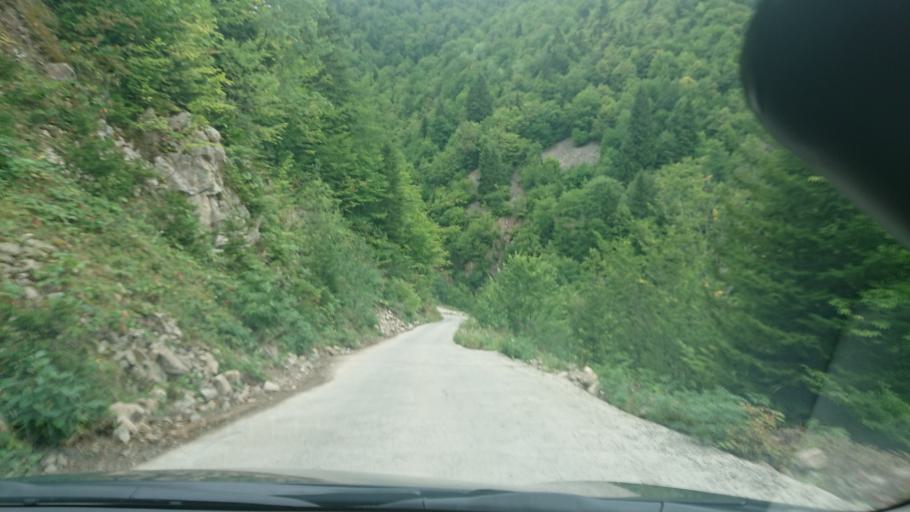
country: TR
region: Gumushane
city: Kurtun
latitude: 40.6864
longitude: 39.0492
